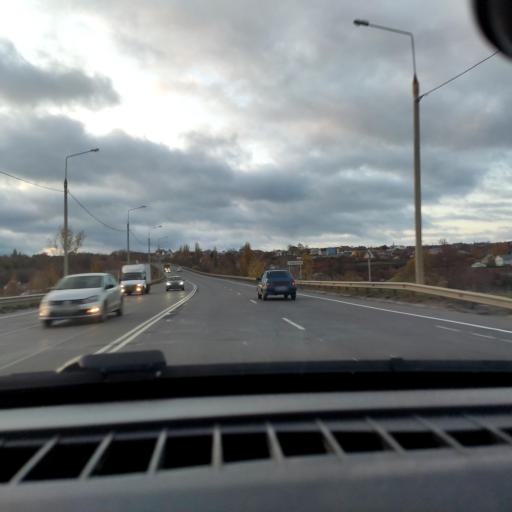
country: RU
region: Voronezj
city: Pridonskoy
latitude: 51.7257
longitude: 39.0556
